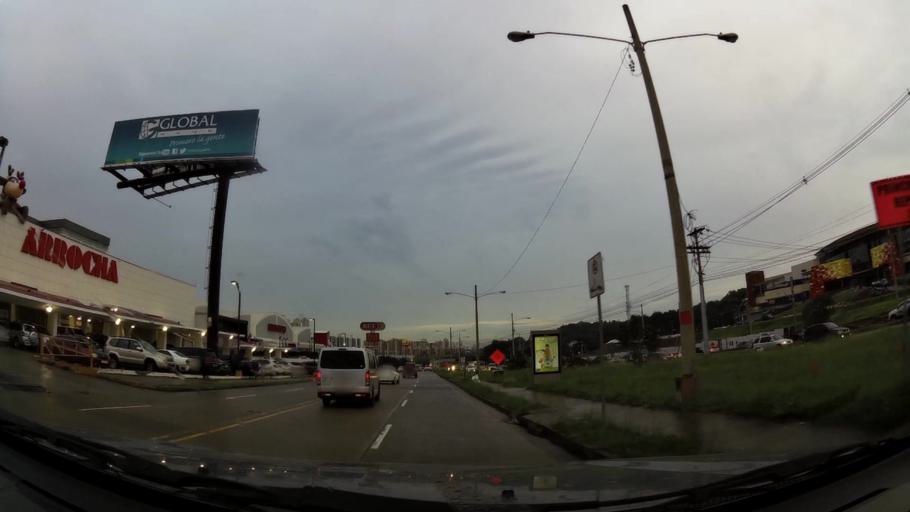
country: PA
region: Panama
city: Panama
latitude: 9.0315
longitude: -79.5338
